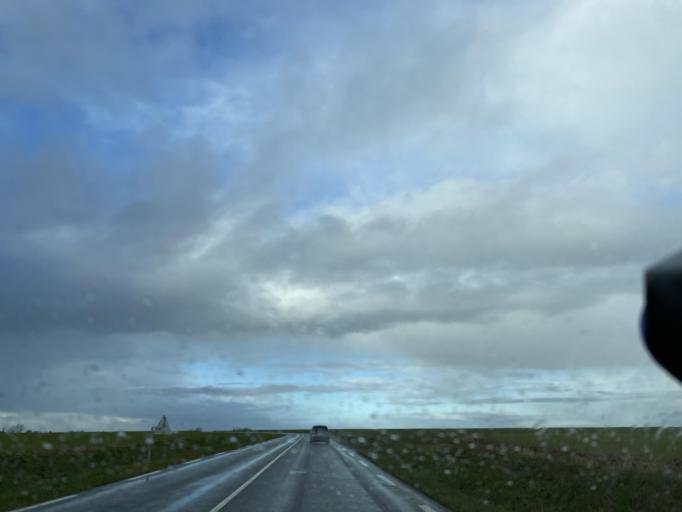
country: FR
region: Centre
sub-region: Departement d'Eure-et-Loir
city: Fontaine-la-Guyon
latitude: 48.5364
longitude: 1.3122
